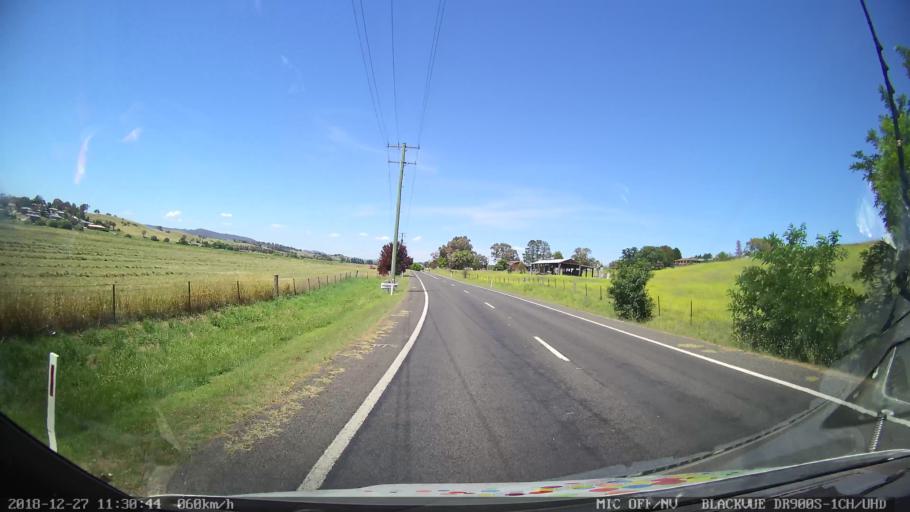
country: AU
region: New South Wales
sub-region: Bathurst Regional
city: Perthville
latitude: -33.4886
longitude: 149.5432
